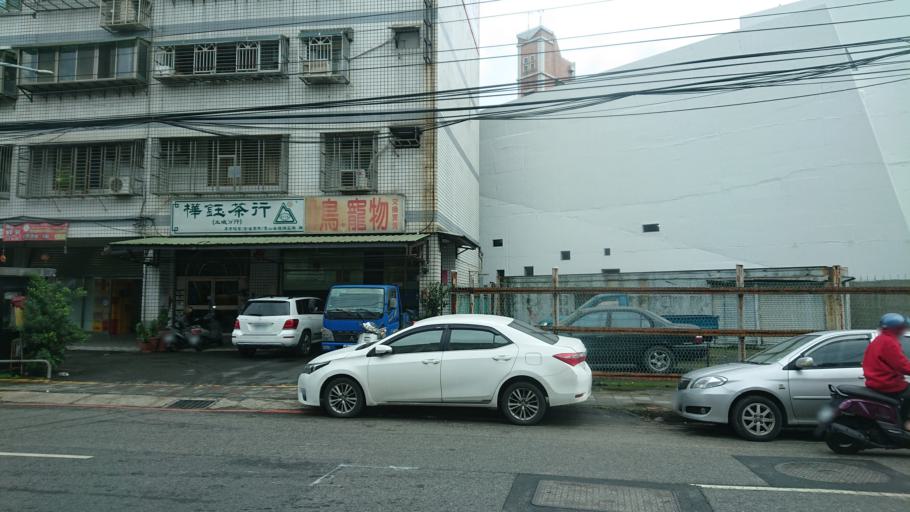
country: TW
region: Taipei
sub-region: Taipei
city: Banqiao
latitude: 24.9516
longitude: 121.4109
